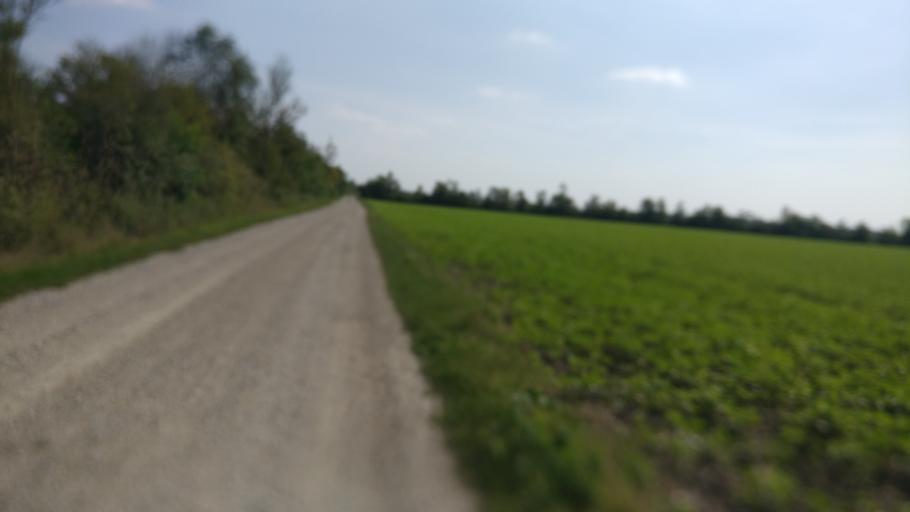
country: AT
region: Lower Austria
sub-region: Politischer Bezirk Modling
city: Munchendorf
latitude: 47.9995
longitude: 16.3955
